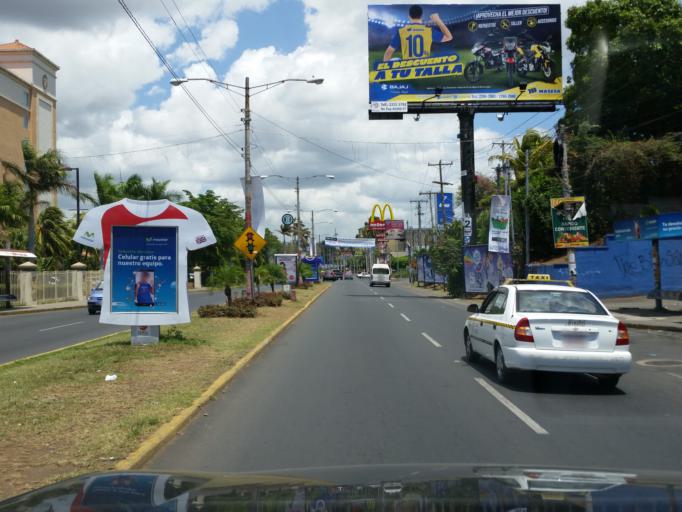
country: NI
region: Managua
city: Managua
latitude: 12.1273
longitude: -86.2658
